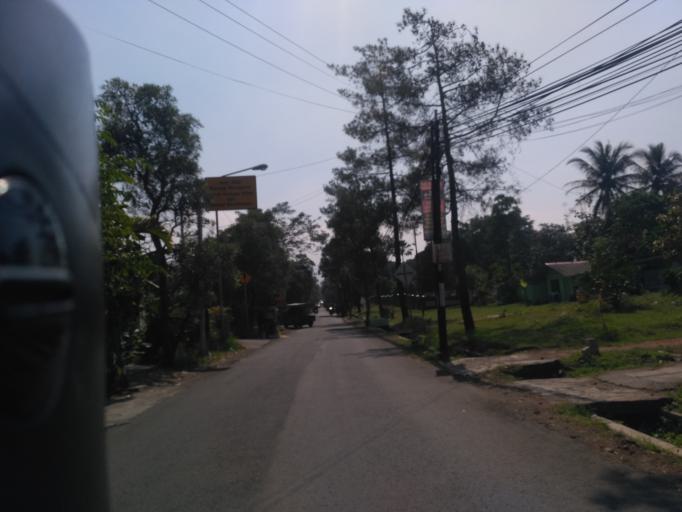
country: ID
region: East Java
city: Batu
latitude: -7.9016
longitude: 112.5813
